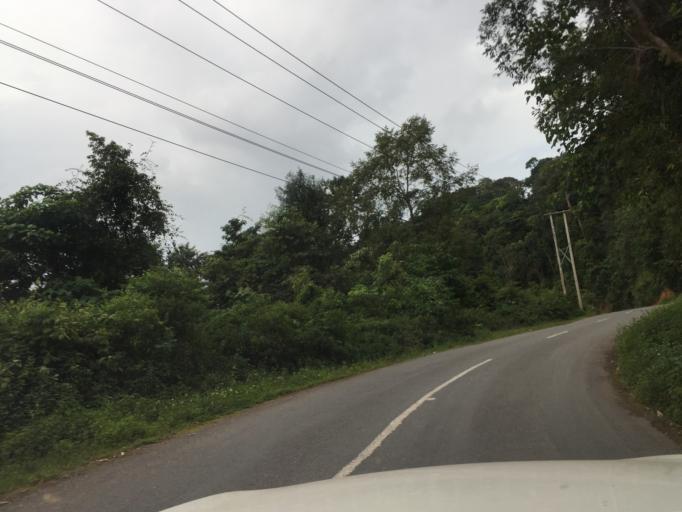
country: LA
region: Phongsali
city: Phongsali
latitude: 21.3352
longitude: 102.0480
